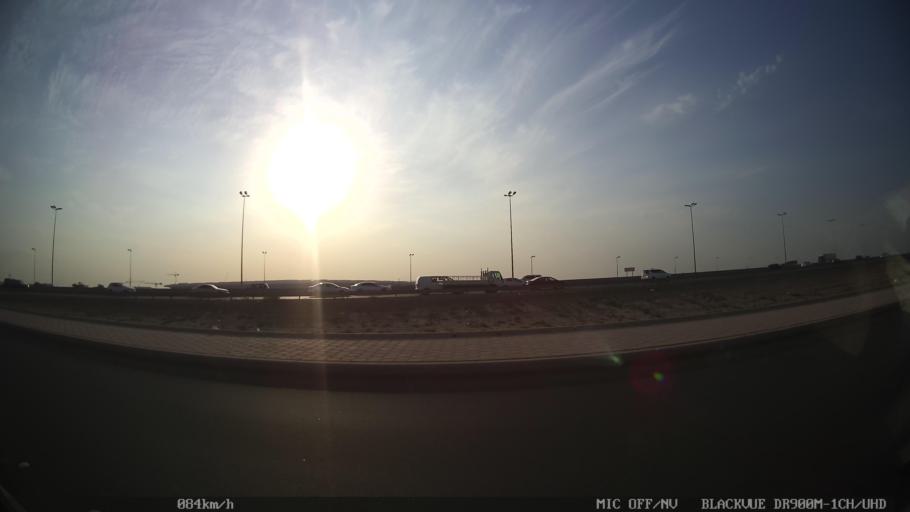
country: KW
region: Al Farwaniyah
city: Janub as Surrah
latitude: 29.2213
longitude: 47.9996
